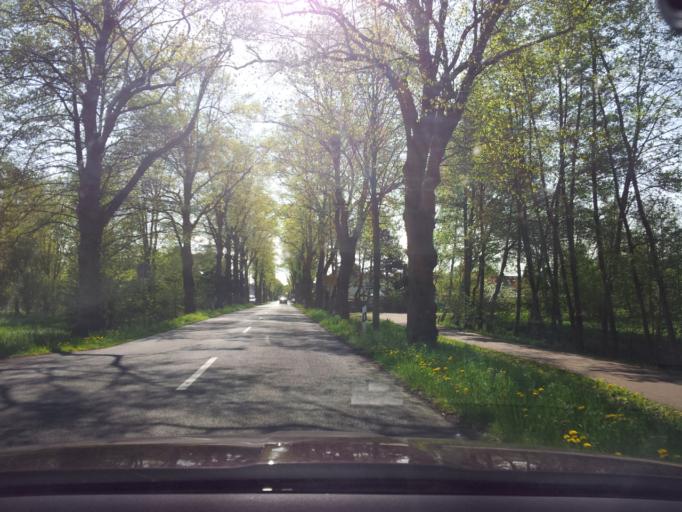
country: DE
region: Brandenburg
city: Juterbog
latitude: 52.0268
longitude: 13.0962
